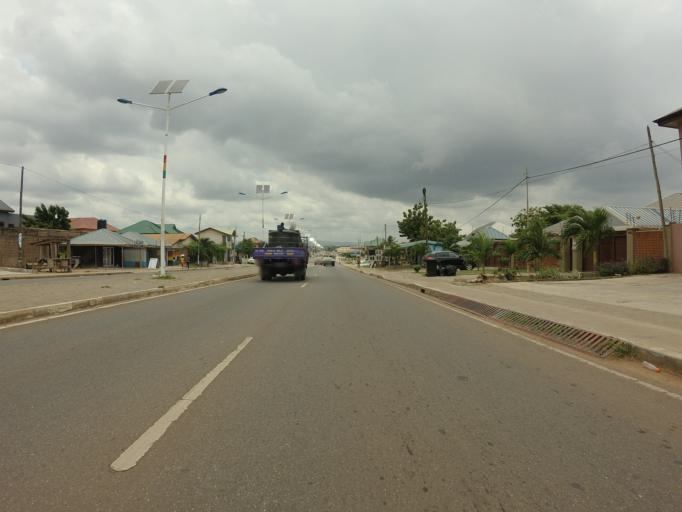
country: GH
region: Greater Accra
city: Medina Estates
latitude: 5.6714
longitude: -0.1515
